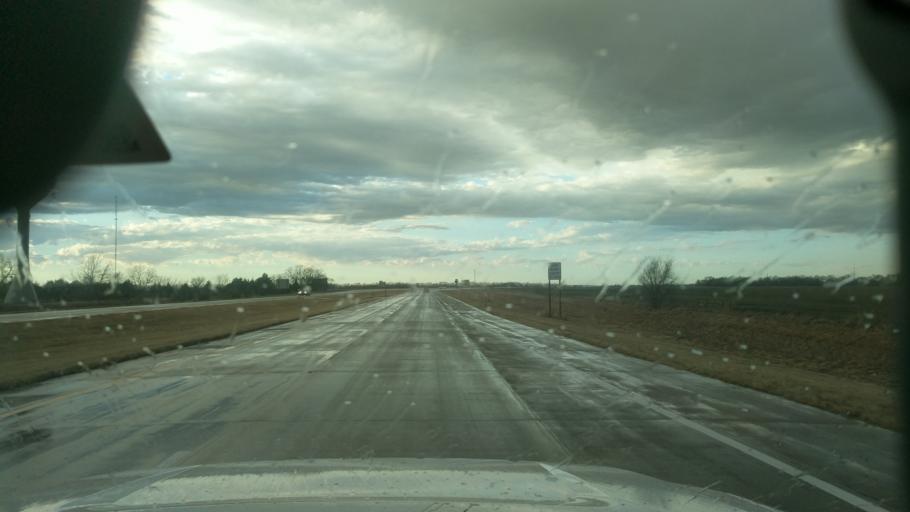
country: US
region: Kansas
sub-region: Harvey County
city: North Newton
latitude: 38.0868
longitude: -97.3512
